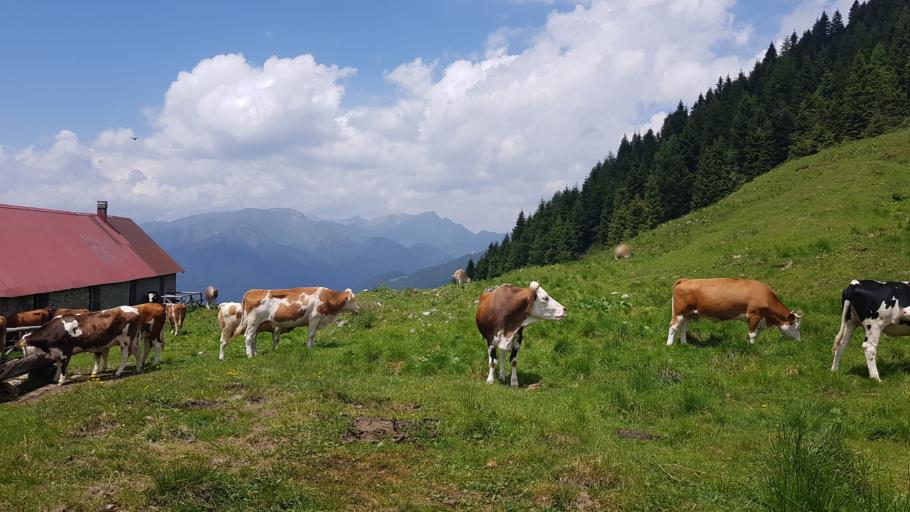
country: IT
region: Friuli Venezia Giulia
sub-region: Provincia di Udine
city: Paularo
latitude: 46.5244
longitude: 13.1812
